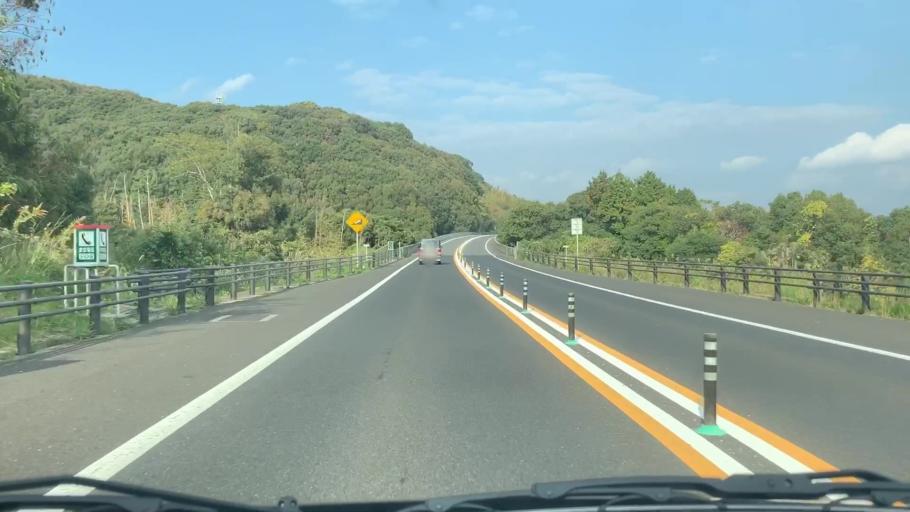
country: JP
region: Nagasaki
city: Sasebo
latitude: 33.0295
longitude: 129.7385
